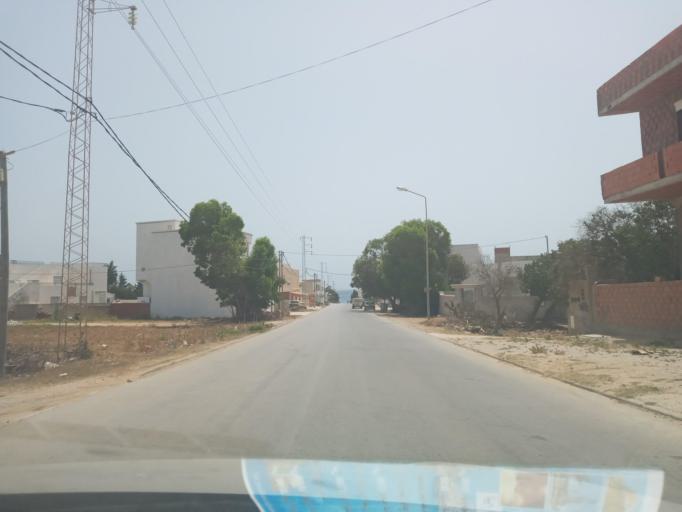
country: TN
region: Nabul
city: El Haouaria
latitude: 37.0368
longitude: 11.0521
